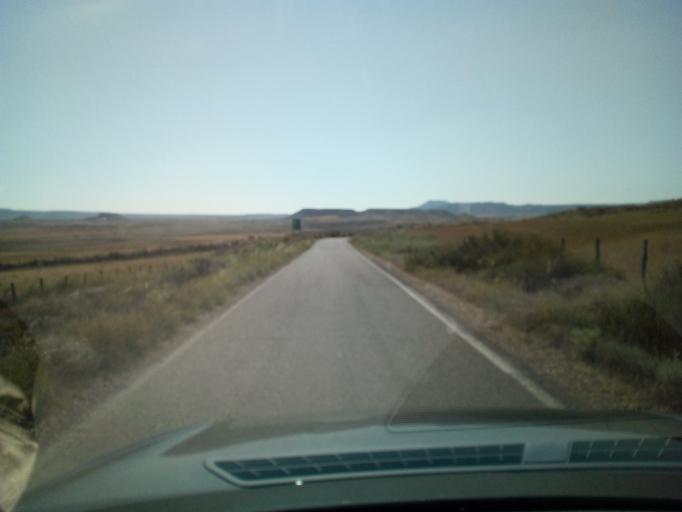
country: ES
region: Navarre
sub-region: Provincia de Navarra
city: Arguedas
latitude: 42.1808
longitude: -1.5284
